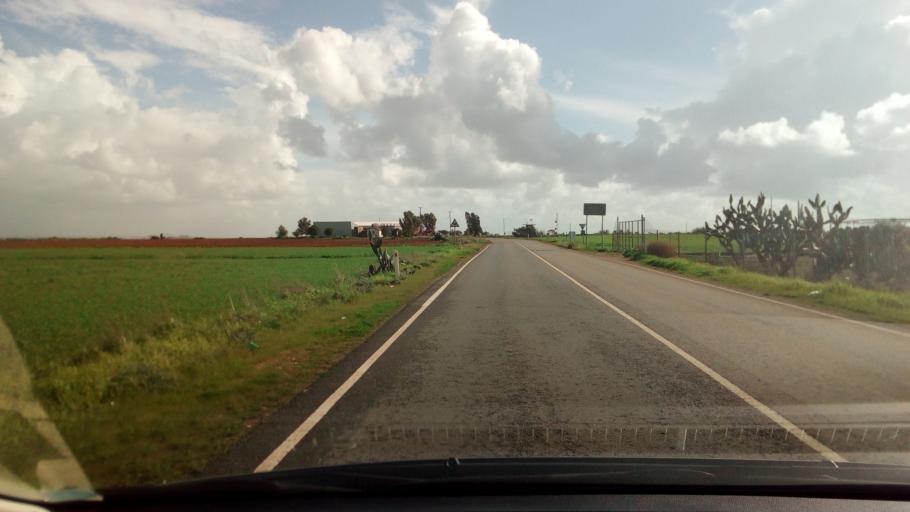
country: CY
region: Ammochostos
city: Achna
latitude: 35.0614
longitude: 33.8026
